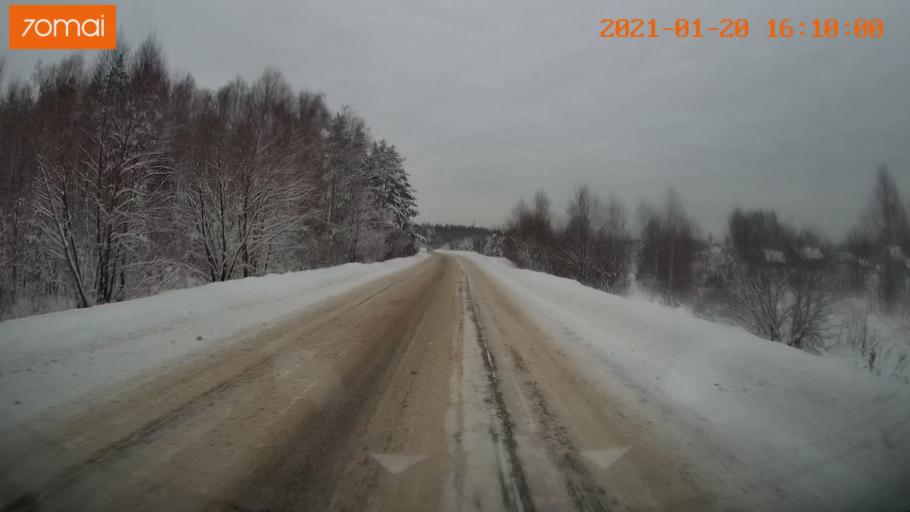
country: RU
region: Vladimir
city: Sudogda
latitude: 56.0873
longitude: 40.7843
